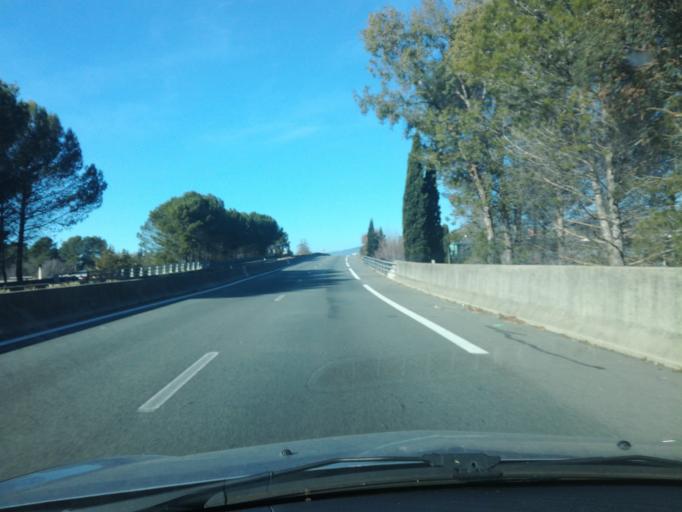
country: FR
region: Provence-Alpes-Cote d'Azur
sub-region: Departement des Alpes-Maritimes
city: Mouans-Sartoux
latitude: 43.6086
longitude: 6.9752
